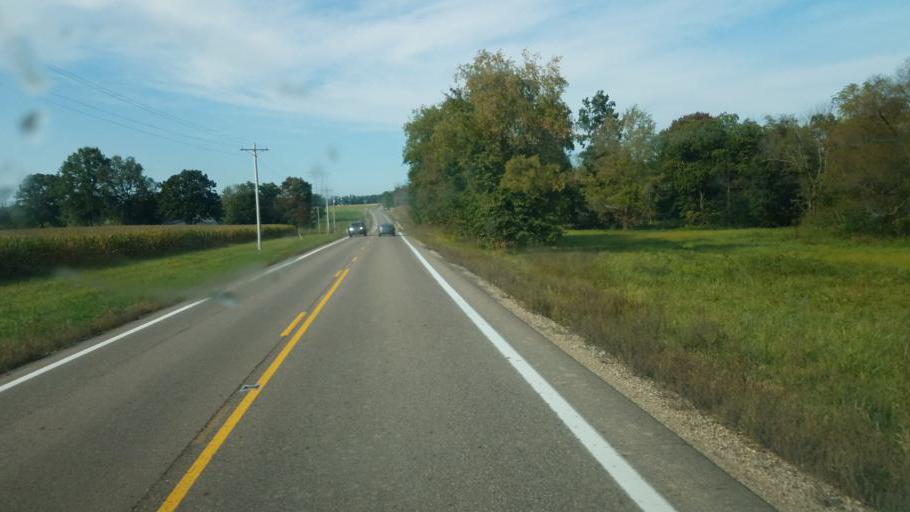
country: US
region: Ohio
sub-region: Knox County
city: Oak Hill
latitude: 40.3408
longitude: -82.3014
